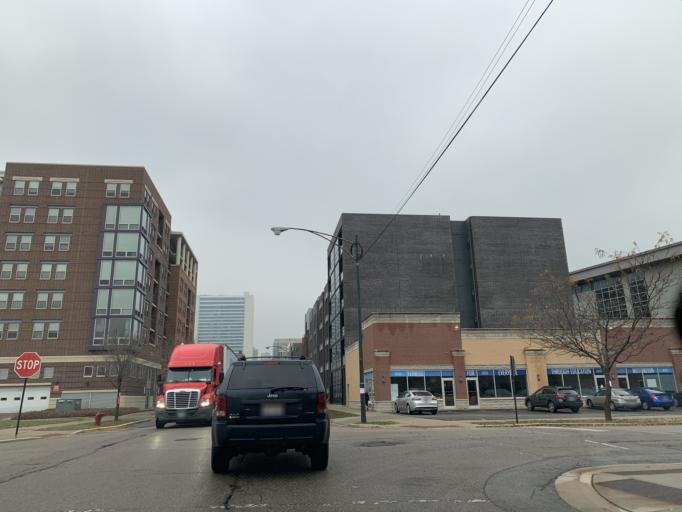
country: US
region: Illinois
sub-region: Cook County
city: Chicago
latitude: 41.9016
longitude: -87.6431
